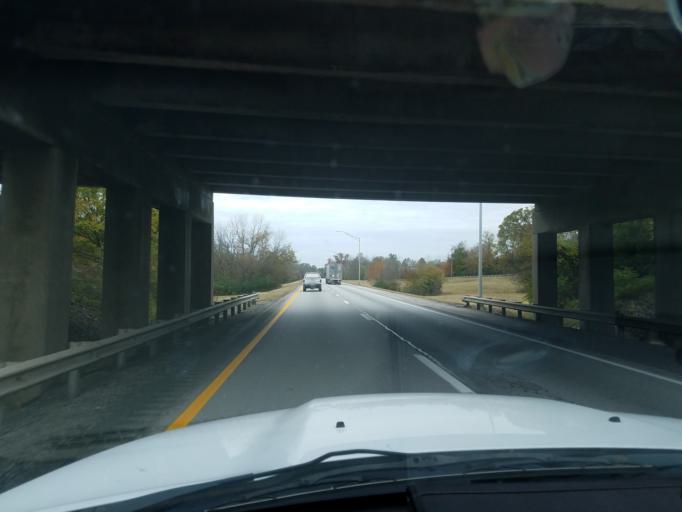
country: US
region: Kentucky
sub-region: Oldham County
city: La Grange
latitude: 38.4001
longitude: -85.3742
